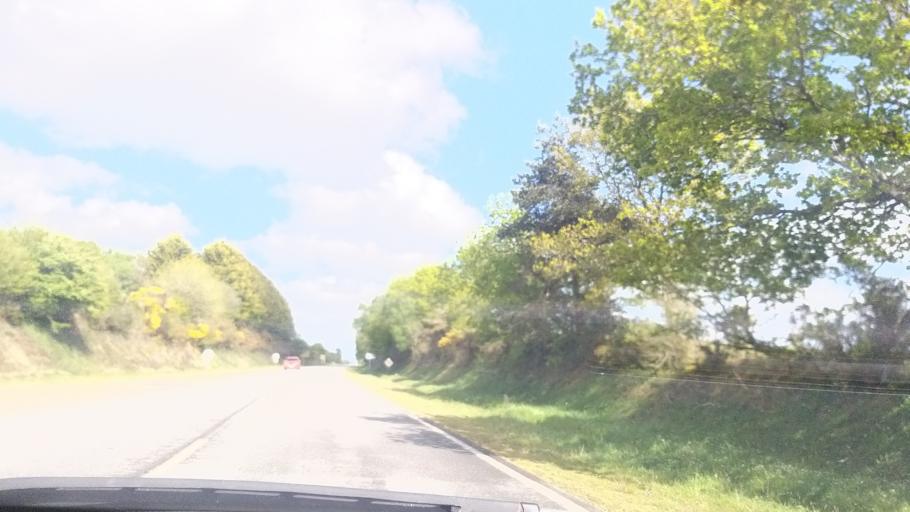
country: FR
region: Brittany
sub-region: Departement du Finistere
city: Huelgoat
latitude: 48.3452
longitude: -3.7458
